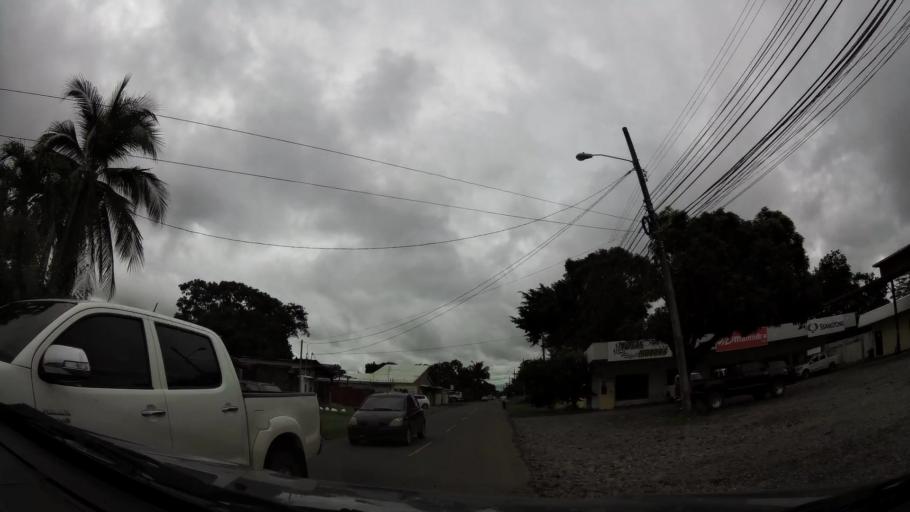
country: PA
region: Chiriqui
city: David
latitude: 8.4293
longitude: -82.4383
